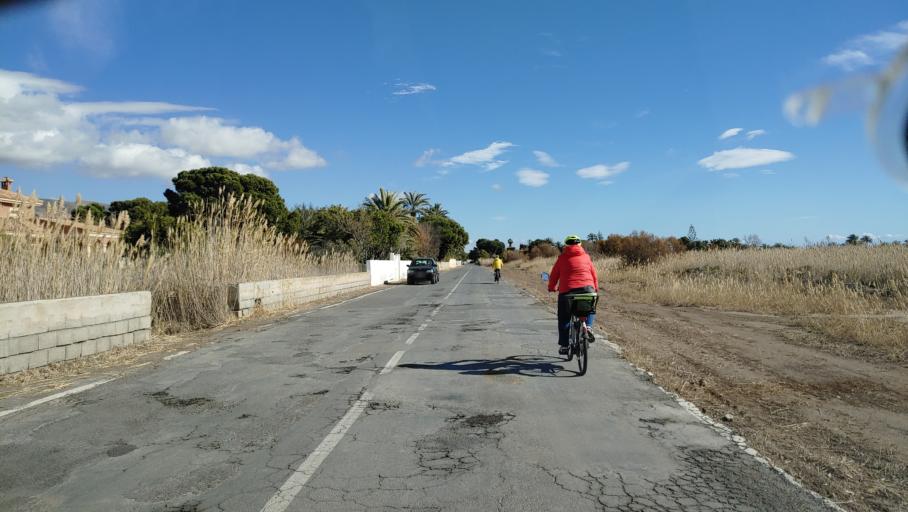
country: ES
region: Andalusia
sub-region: Provincia de Almeria
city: Aguadulce
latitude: 36.7922
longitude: -2.5921
